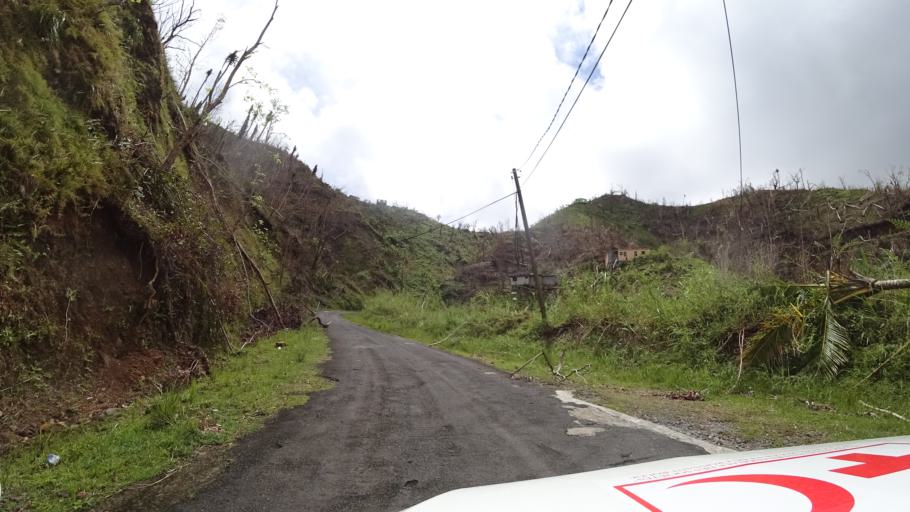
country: DM
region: Saint David
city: Rosalie
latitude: 15.3965
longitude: -61.2588
